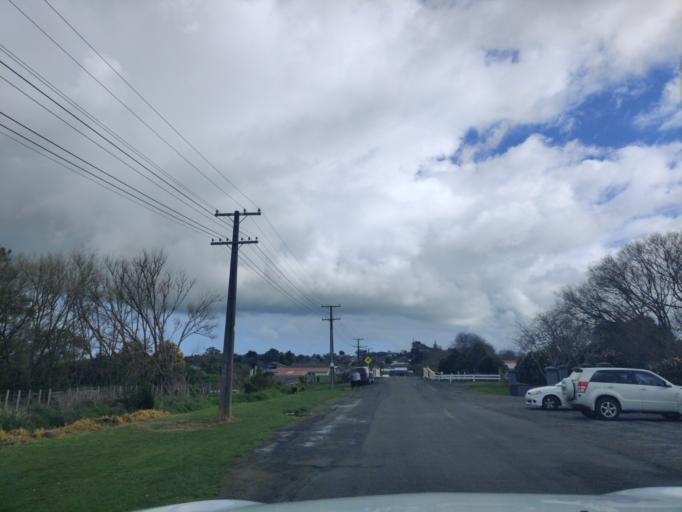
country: NZ
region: Manawatu-Wanganui
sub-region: Palmerston North City
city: Palmerston North
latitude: -40.2327
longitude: 175.5569
